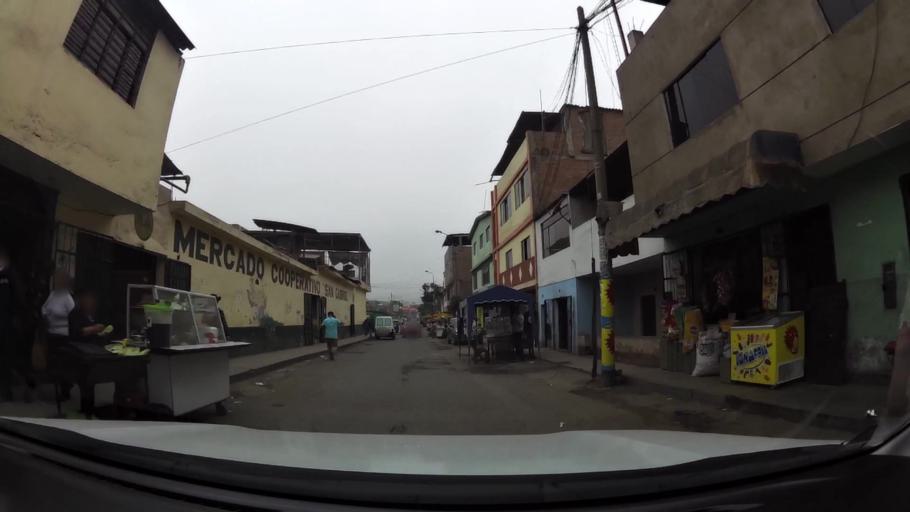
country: PE
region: Lima
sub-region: Lima
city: Surco
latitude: -12.1563
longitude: -76.9586
